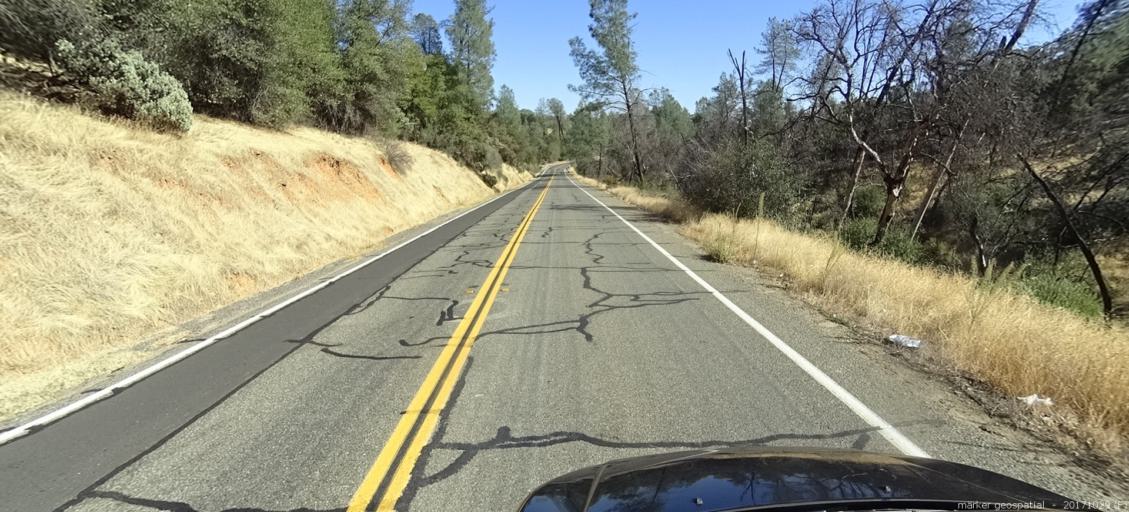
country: US
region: California
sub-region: Shasta County
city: Shasta
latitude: 40.4902
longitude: -122.5315
